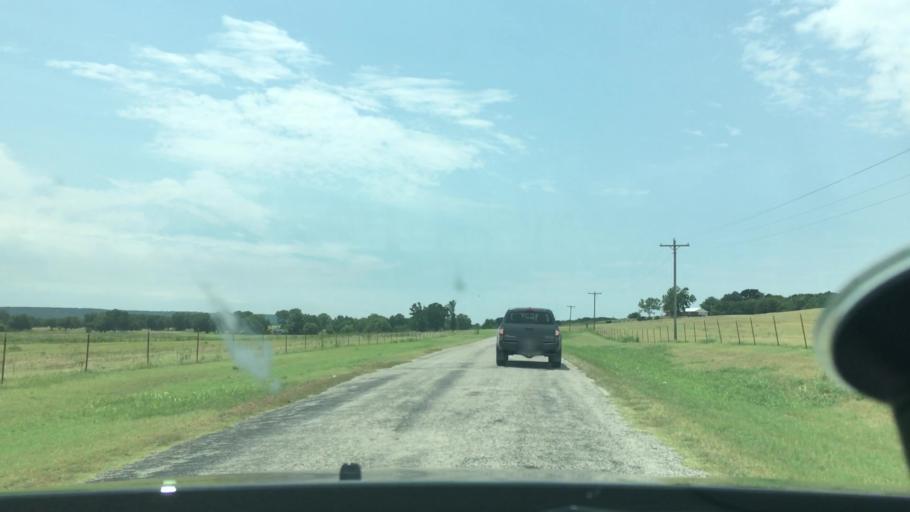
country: US
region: Texas
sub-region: Cooke County
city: Muenster
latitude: 33.8891
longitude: -97.3533
